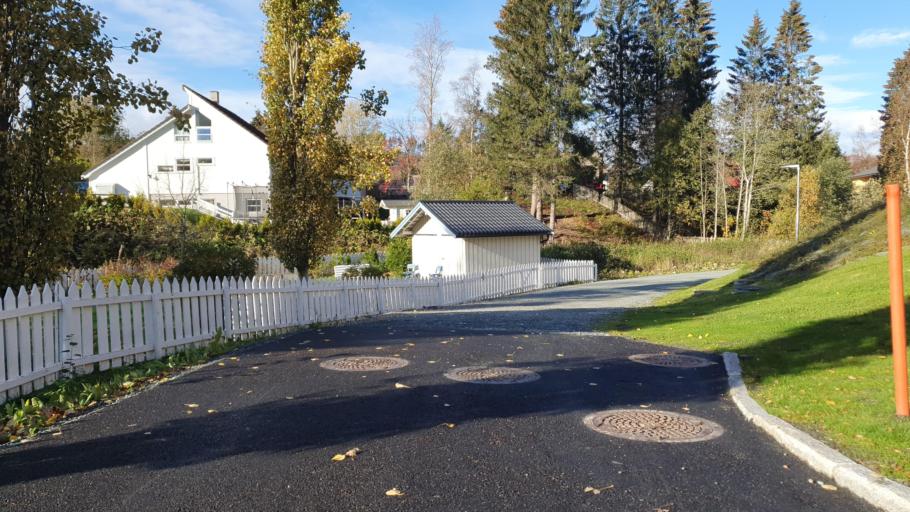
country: NO
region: Sor-Trondelag
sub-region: Klaebu
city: Klaebu
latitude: 63.2994
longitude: 10.4802
